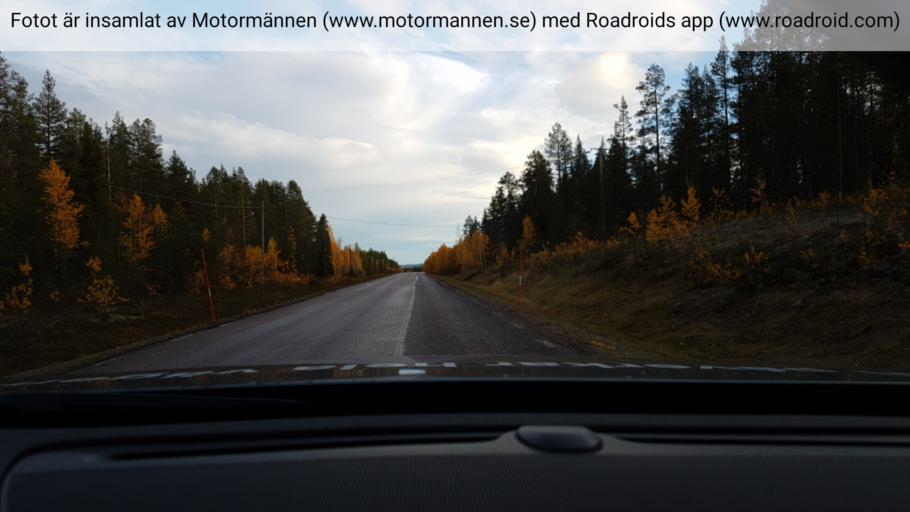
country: SE
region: Norrbotten
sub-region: Overkalix Kommun
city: OEverkalix
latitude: 67.0229
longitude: 22.5177
